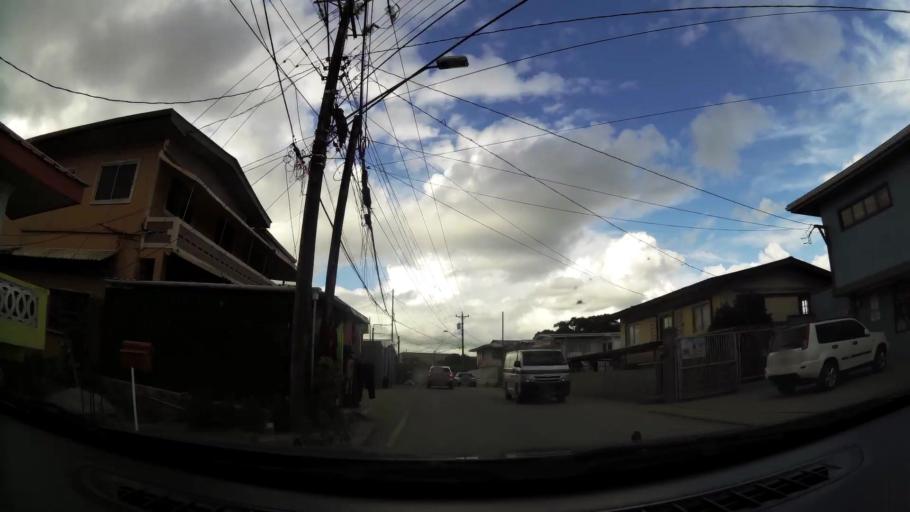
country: TT
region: City of San Fernando
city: Mon Repos
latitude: 10.2717
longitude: -61.4386
